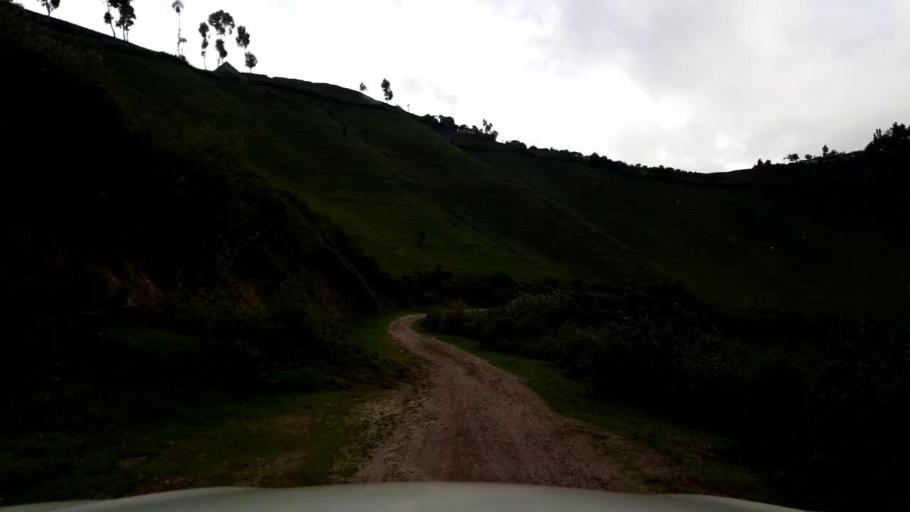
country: RW
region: Western Province
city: Gisenyi
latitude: -1.6770
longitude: 29.4155
